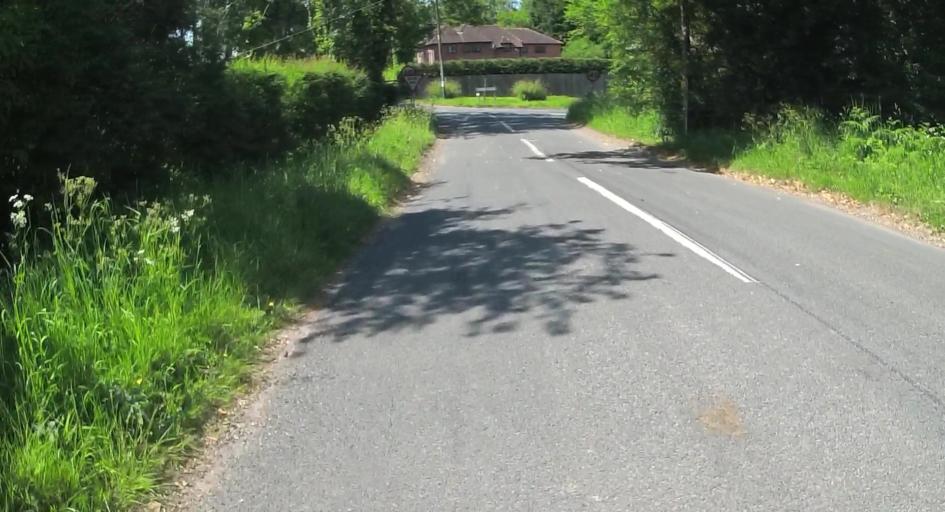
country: GB
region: England
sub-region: Hampshire
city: Kingsclere
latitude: 51.3468
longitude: -1.2062
